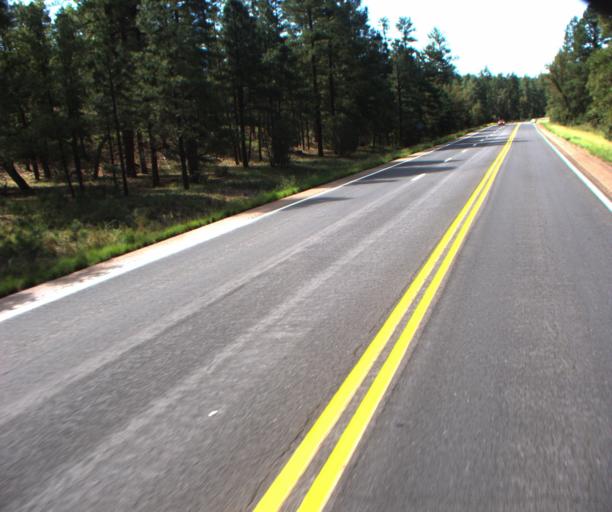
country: US
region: Arizona
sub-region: Navajo County
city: Show Low
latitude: 34.1881
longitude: -110.0918
